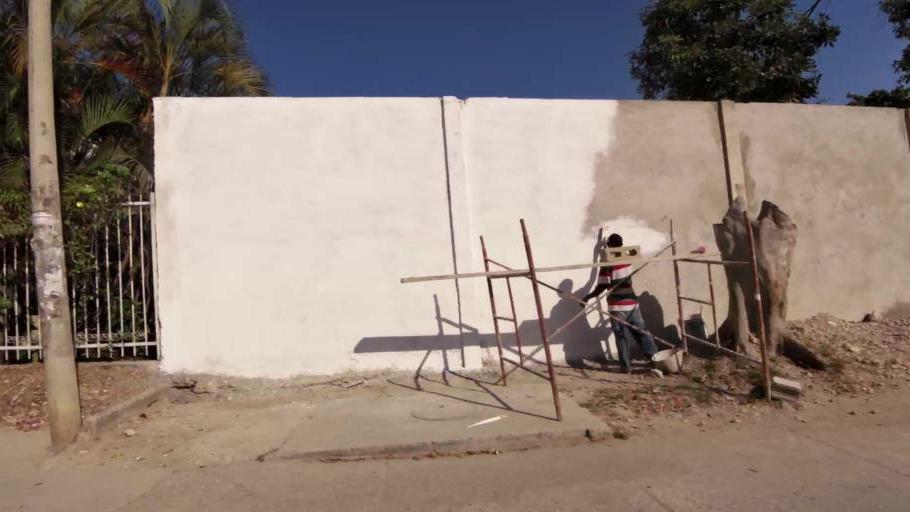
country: CO
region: Bolivar
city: Cartagena
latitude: 10.3859
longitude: -75.4855
